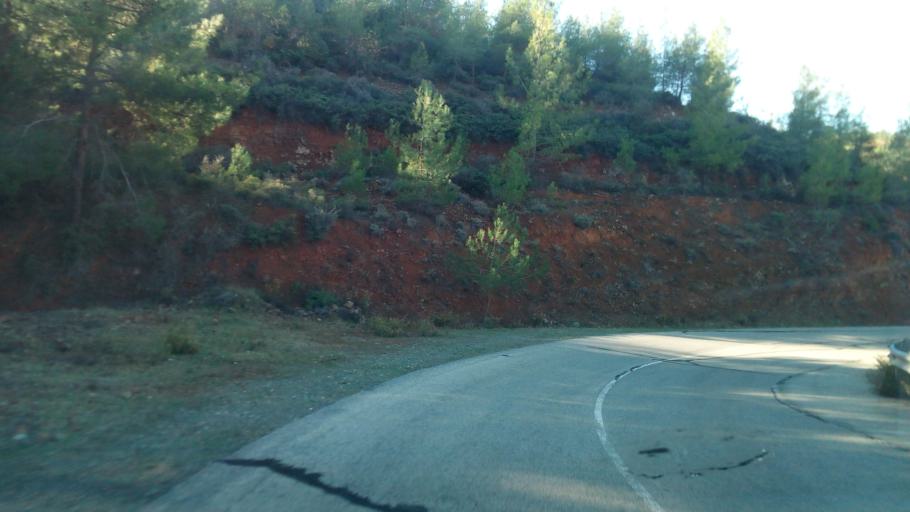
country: CY
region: Lefkosia
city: Lefka
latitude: 35.0672
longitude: 32.8169
